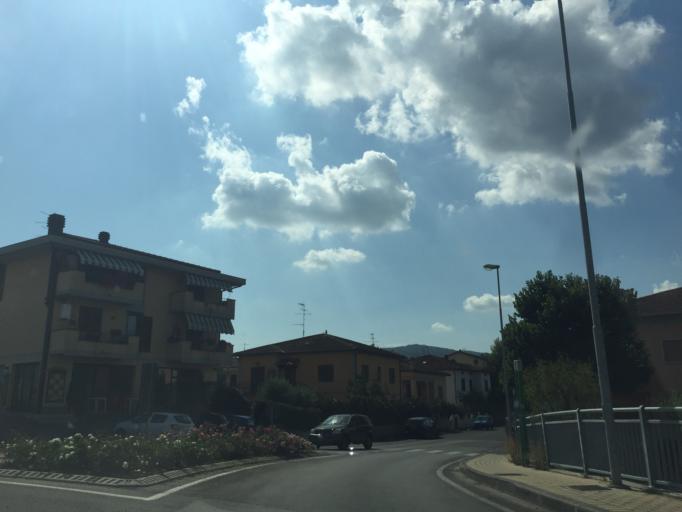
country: IT
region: Tuscany
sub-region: Provincia di Pistoia
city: Cantagrillo-Casalguidi
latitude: 43.8831
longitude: 10.9165
